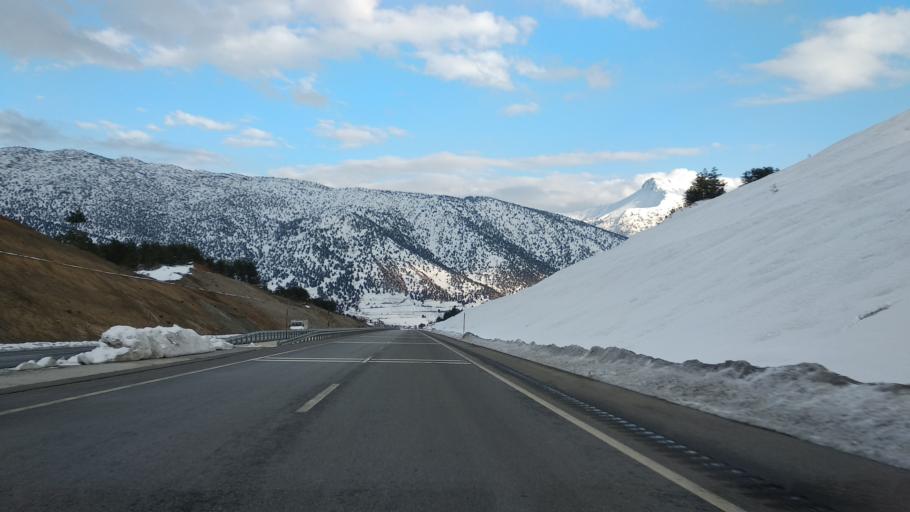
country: TR
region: Kahramanmaras
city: Goksun
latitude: 37.9053
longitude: 36.5990
